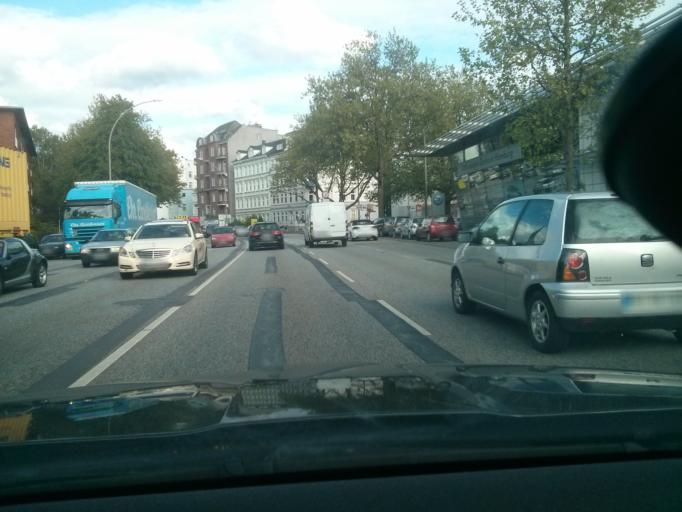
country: DE
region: Hamburg
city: St. Pauli
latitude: 53.5697
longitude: 9.9590
